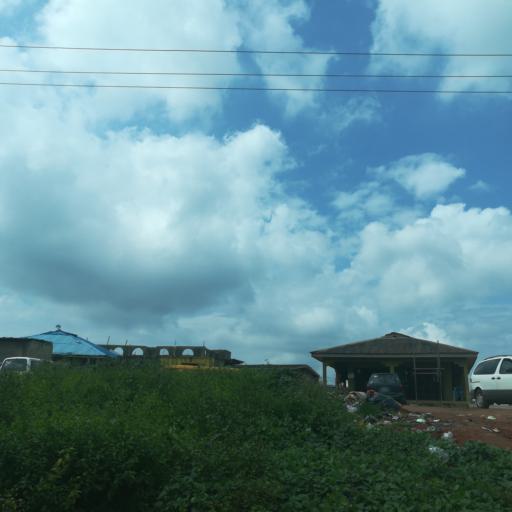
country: NG
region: Lagos
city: Ejirin
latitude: 6.6497
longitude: 3.7099
